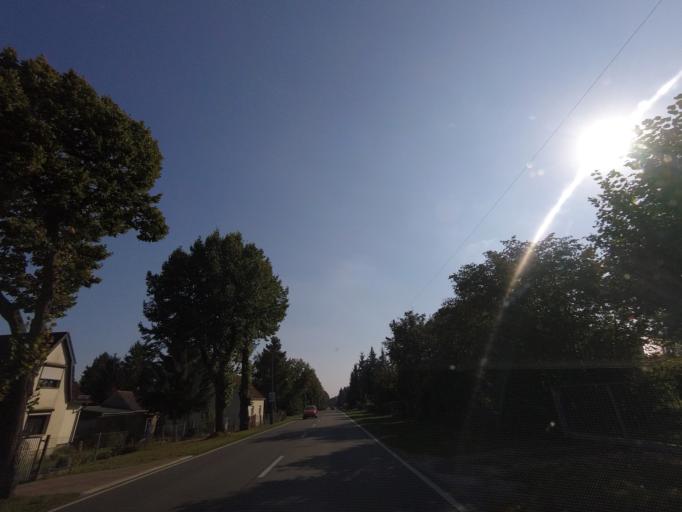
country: DE
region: Saxony-Anhalt
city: Jessen
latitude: 51.8016
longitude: 13.0166
